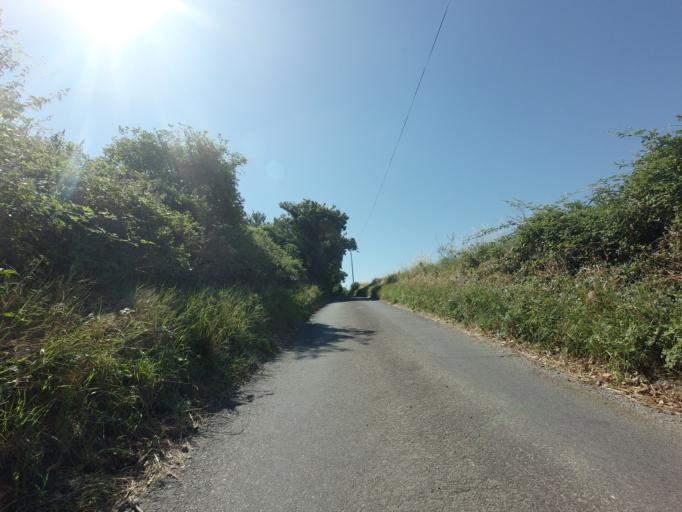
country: GB
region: England
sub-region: Kent
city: Dartford
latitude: 51.4116
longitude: 0.2053
